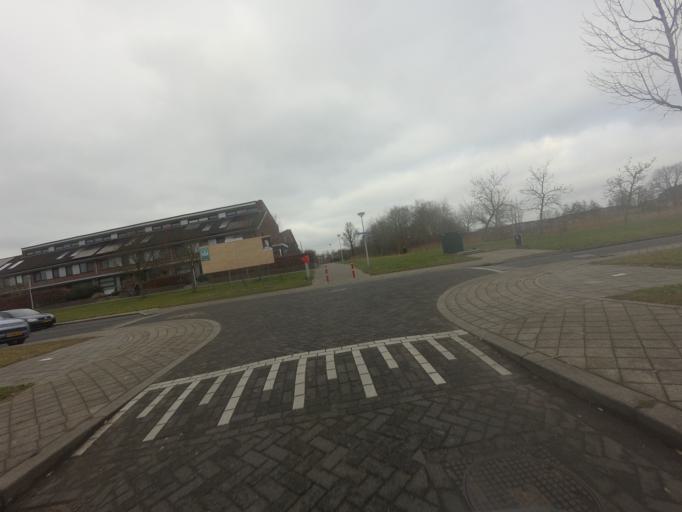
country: NL
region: Utrecht
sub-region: Stichtse Vecht
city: Spechtenkamp
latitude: 52.0805
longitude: 5.0148
